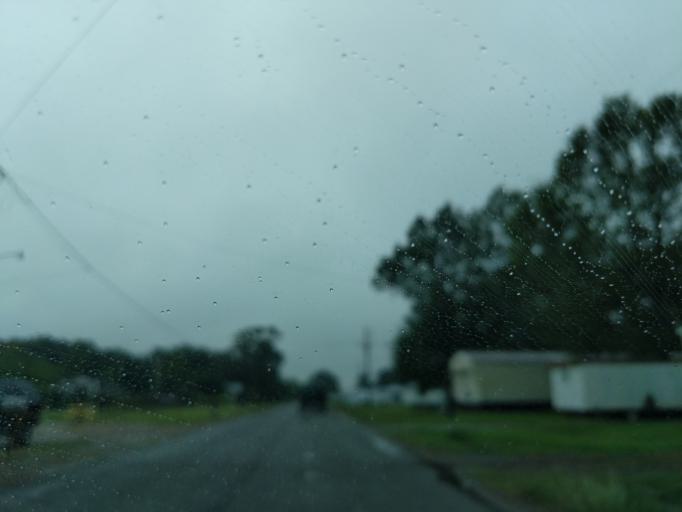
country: US
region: Louisiana
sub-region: Vermilion Parish
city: Kaplan
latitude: 29.9950
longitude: -92.2819
